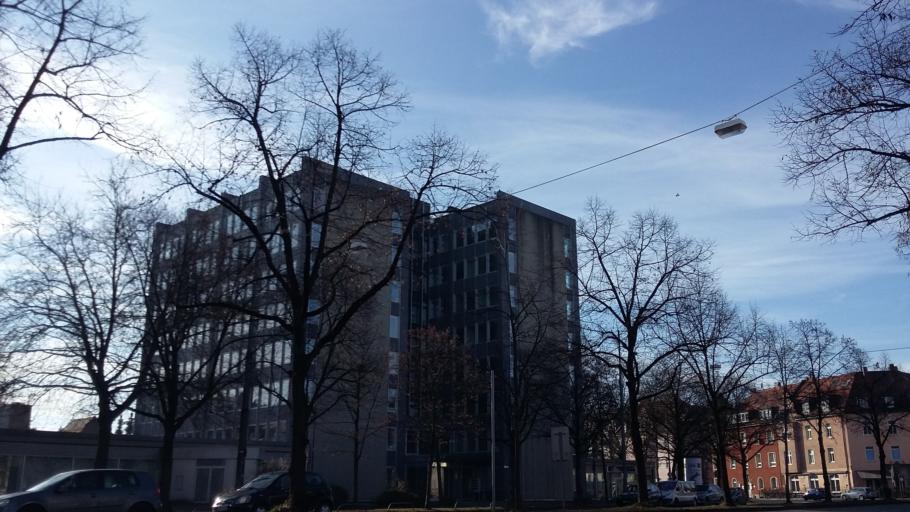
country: DE
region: Bavaria
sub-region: Upper Bavaria
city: Pasing
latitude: 48.1545
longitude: 11.5110
